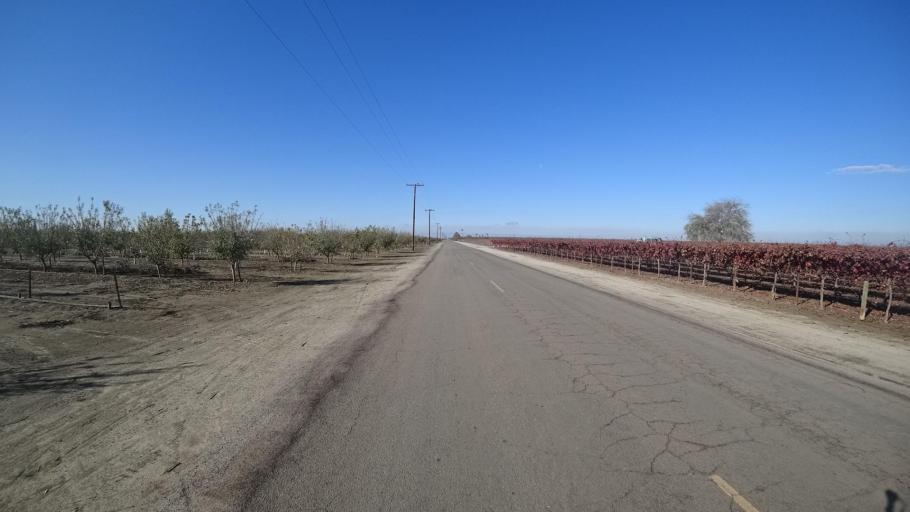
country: US
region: California
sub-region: Kern County
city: Delano
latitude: 35.7323
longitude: -119.2528
